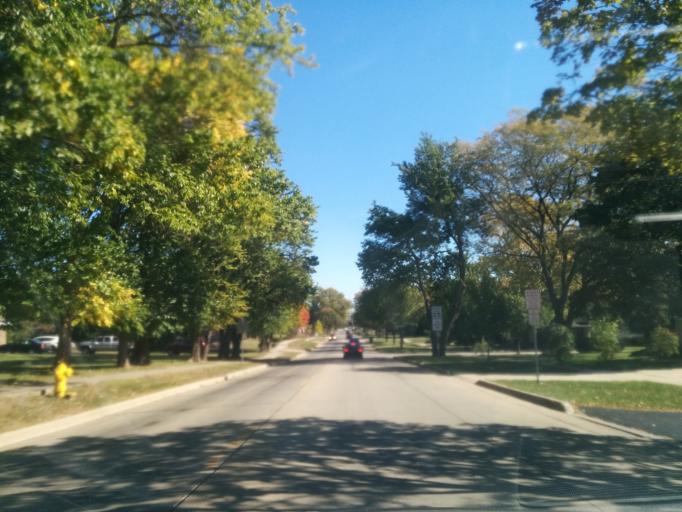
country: US
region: Illinois
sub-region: DuPage County
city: Lombard
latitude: 41.8750
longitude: -88.0105
